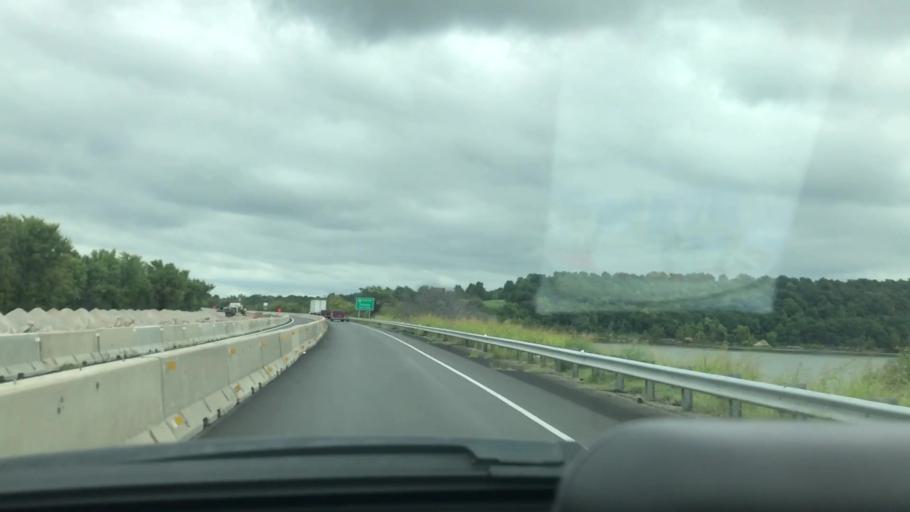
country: US
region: Oklahoma
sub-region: McIntosh County
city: Eufaula
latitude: 35.2441
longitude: -95.5857
